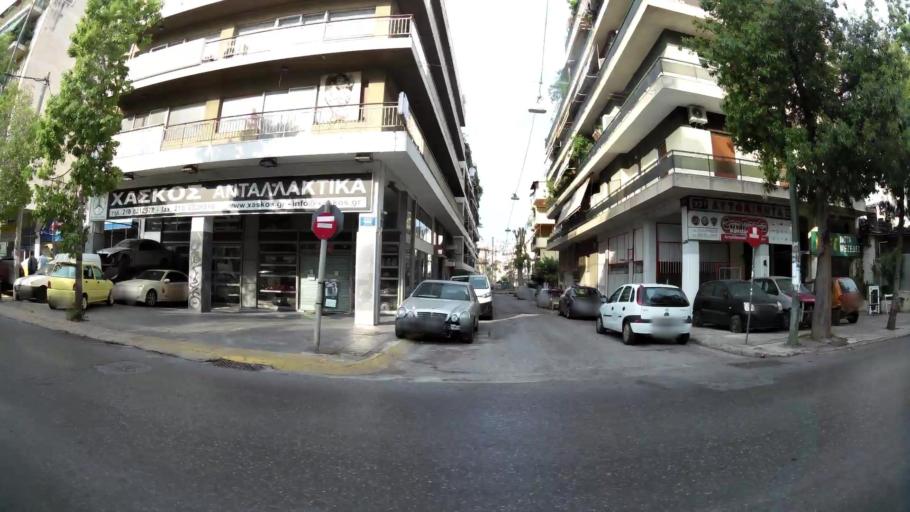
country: GR
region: Attica
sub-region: Nomarchia Athinas
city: Kipseli
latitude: 38.0058
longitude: 23.7222
